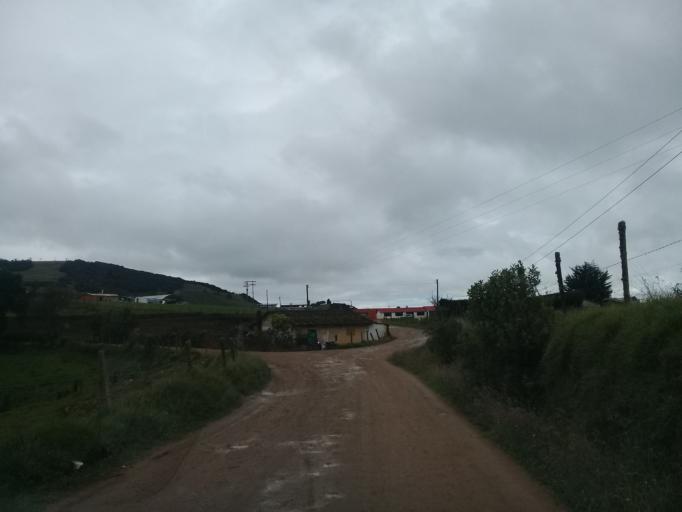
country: CO
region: Boyaca
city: Samaca
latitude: 5.4531
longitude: -73.4405
